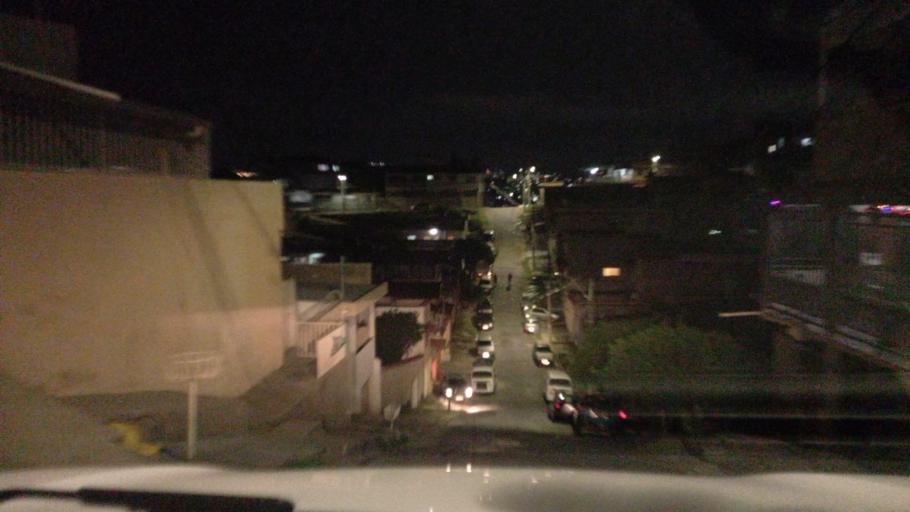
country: BR
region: Minas Gerais
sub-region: Belo Horizonte
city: Belo Horizonte
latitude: -19.8786
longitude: -43.9436
